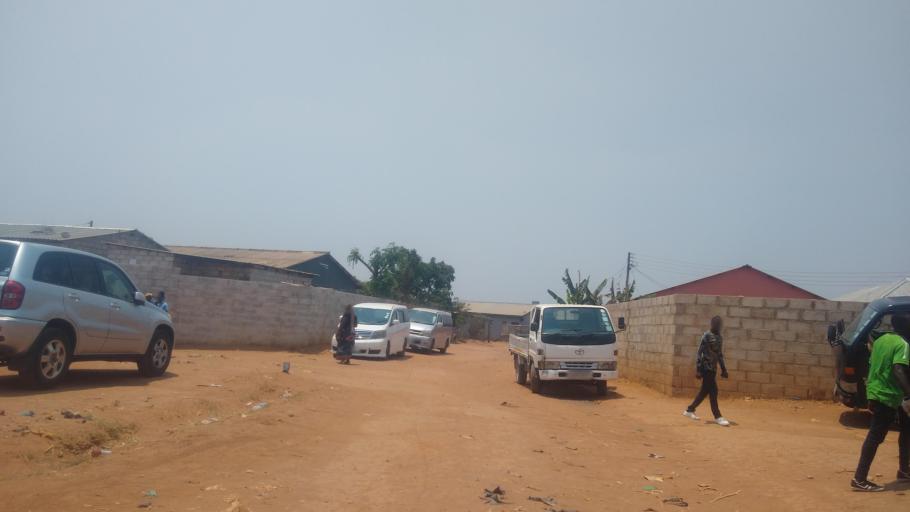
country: ZM
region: Lusaka
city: Lusaka
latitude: -15.4376
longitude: 28.3767
